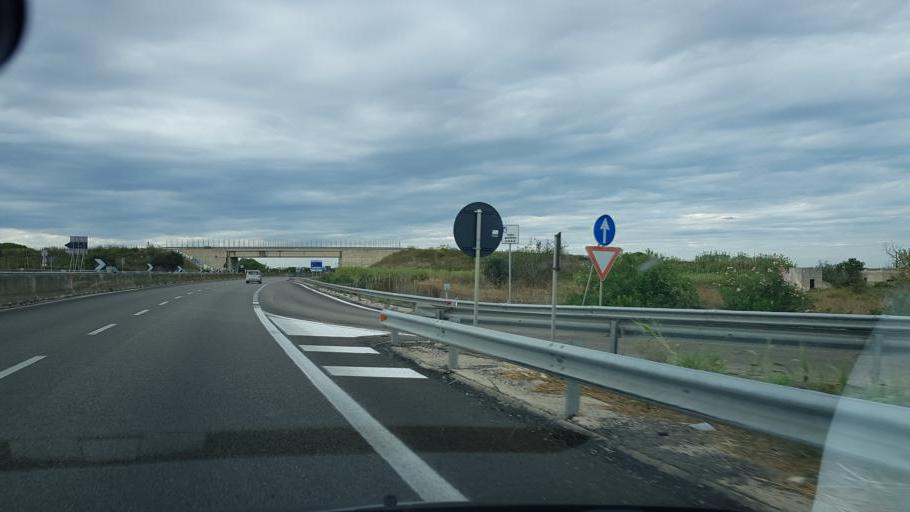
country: IT
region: Apulia
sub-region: Provincia di Lecce
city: Surbo
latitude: 40.3875
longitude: 18.1233
